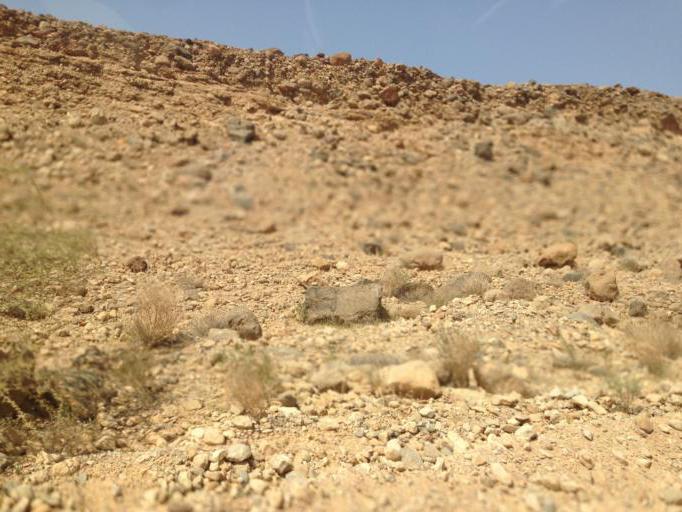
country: OM
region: Ash Sharqiyah
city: Ibra'
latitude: 23.0756
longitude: 58.8777
